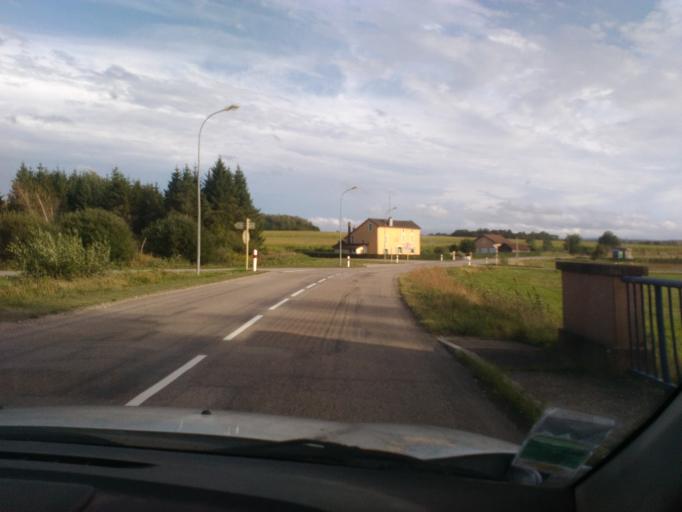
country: FR
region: Lorraine
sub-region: Departement des Vosges
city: Jeanmenil
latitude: 48.3281
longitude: 6.6777
